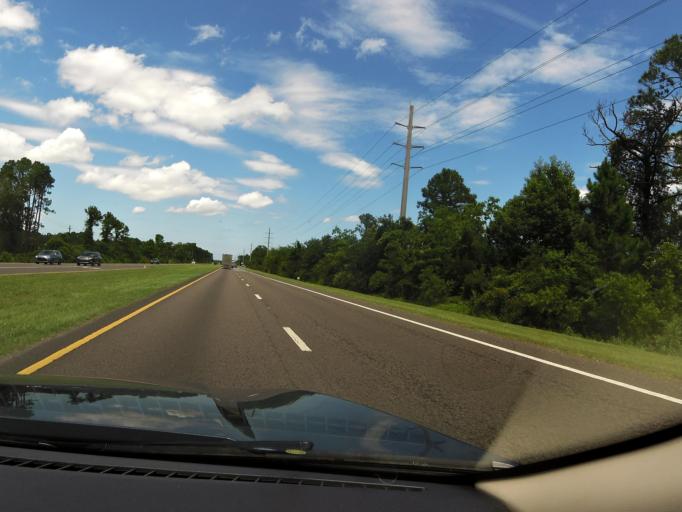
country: US
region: Florida
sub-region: Nassau County
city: Fernandina Beach
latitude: 30.6163
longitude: -81.5057
